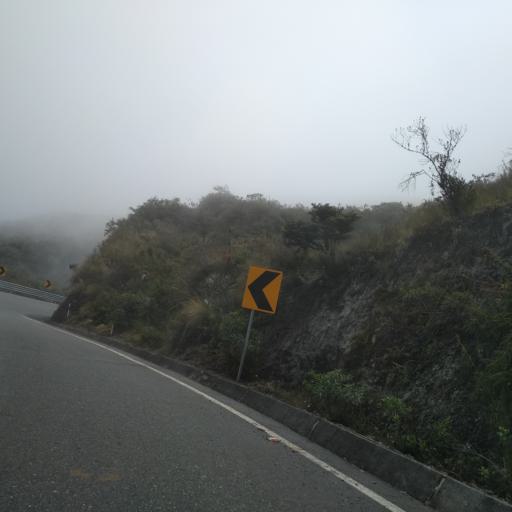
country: EC
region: Cotopaxi
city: La Mana
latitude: -0.9872
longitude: -78.9691
